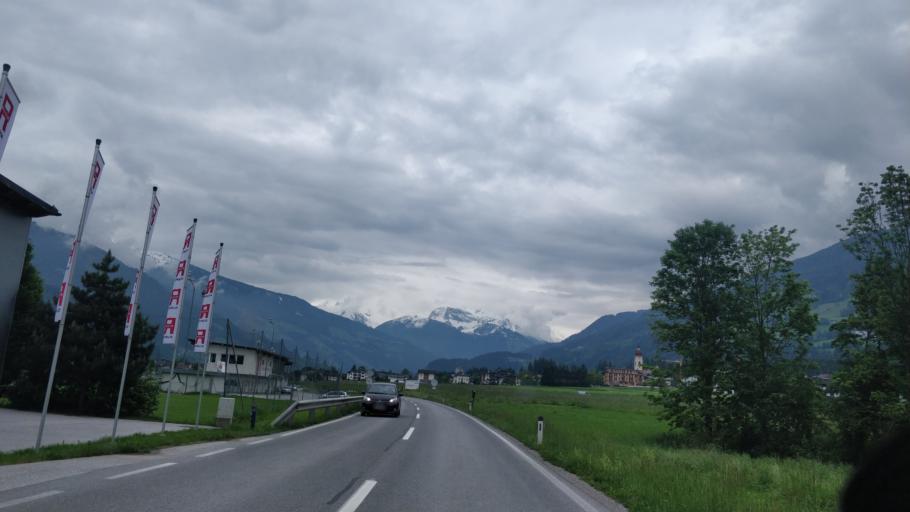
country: AT
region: Tyrol
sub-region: Politischer Bezirk Schwaz
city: Ried im Zillertal
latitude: 47.3077
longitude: 11.8682
